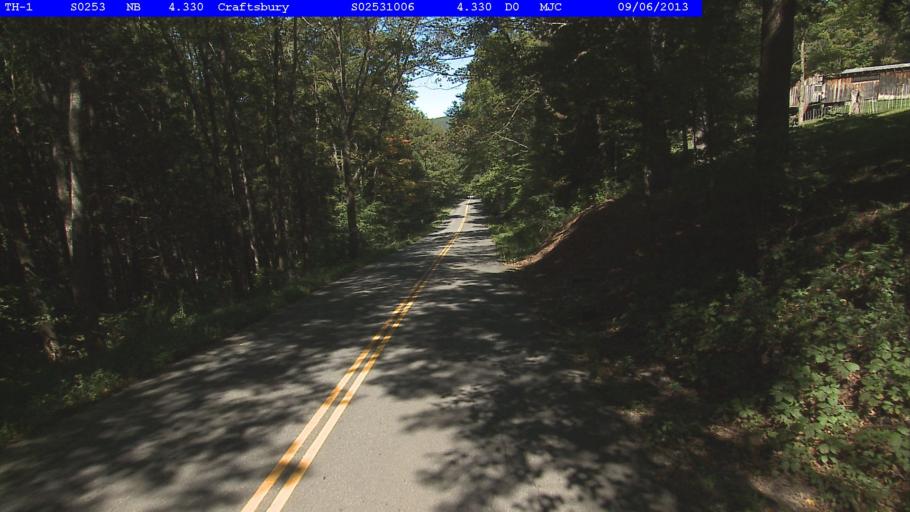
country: US
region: Vermont
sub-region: Caledonia County
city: Hardwick
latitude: 44.6681
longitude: -72.3895
